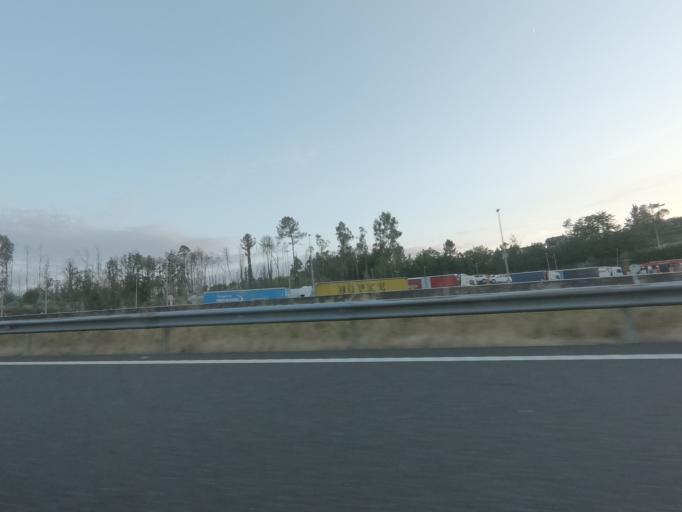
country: ES
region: Galicia
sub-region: Provincia de Pontevedra
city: Ponteareas
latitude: 42.1453
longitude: -8.4750
